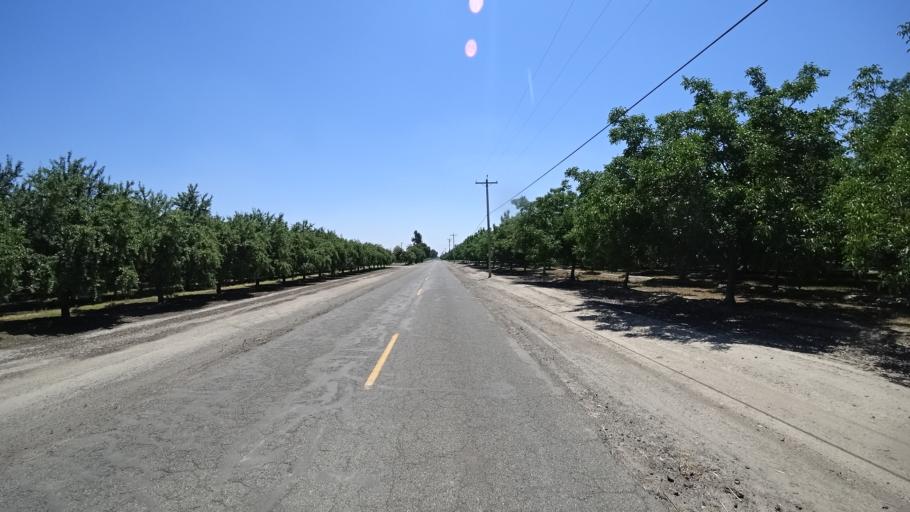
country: US
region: California
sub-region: Kings County
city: Lucerne
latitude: 36.4136
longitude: -119.6189
